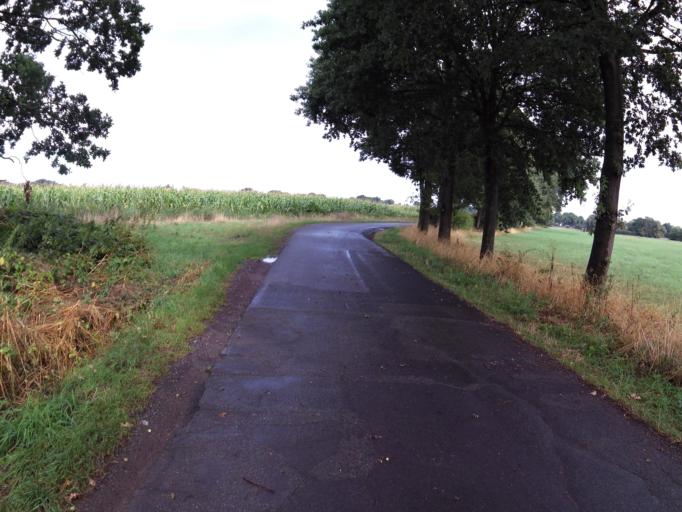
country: DE
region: Lower Saxony
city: Marklohe
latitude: 52.6821
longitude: 9.1721
